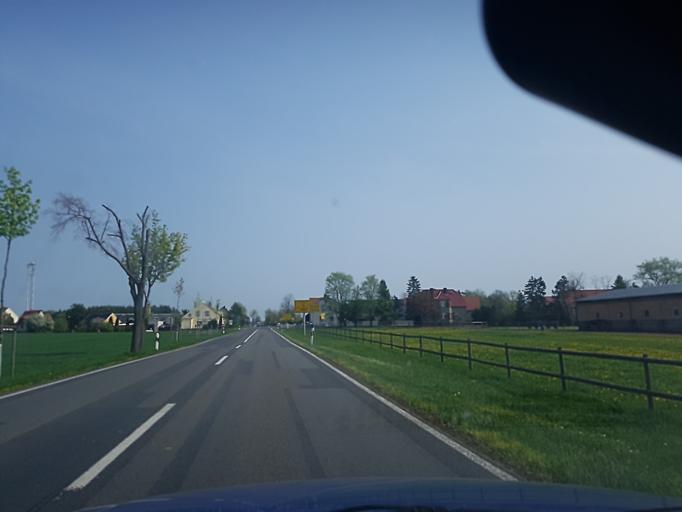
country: DE
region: Saxony
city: Arzberg
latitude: 51.5978
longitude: 13.1241
